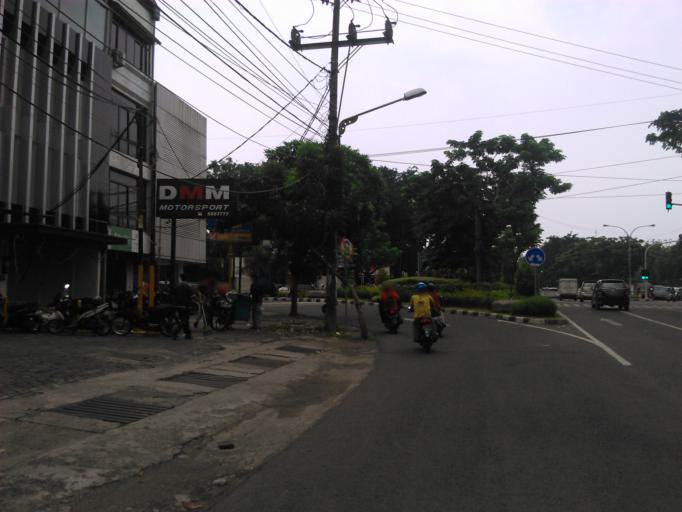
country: ID
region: East Java
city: Gubengairlangga
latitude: -7.2791
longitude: 112.7617
